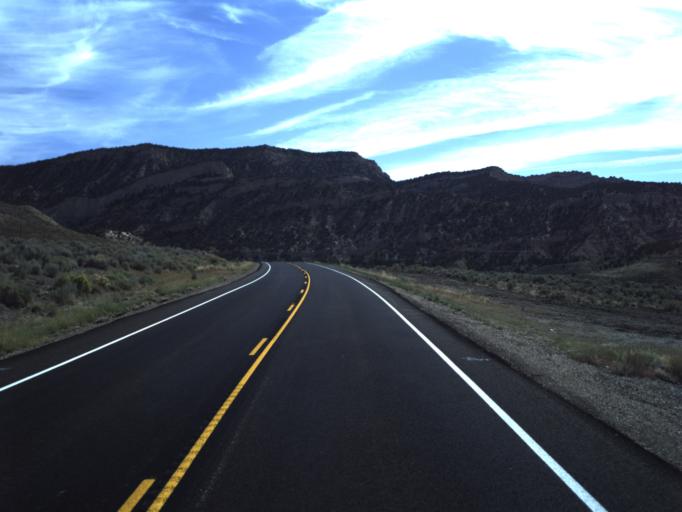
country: US
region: Utah
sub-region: Garfield County
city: Panguitch
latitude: 37.5948
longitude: -111.9424
